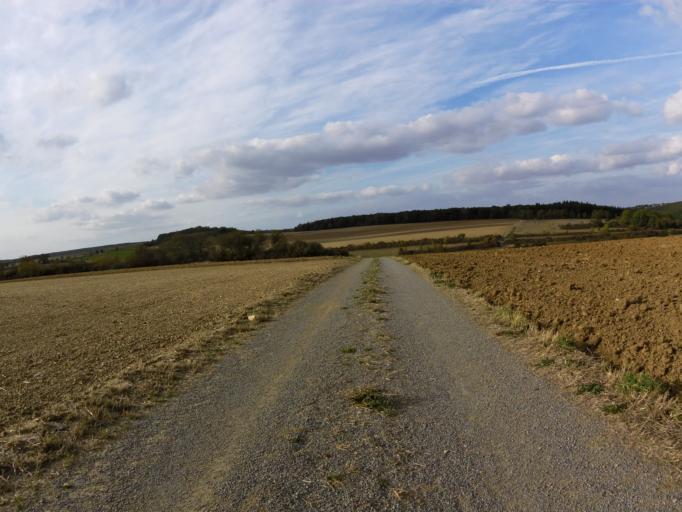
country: DE
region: Bavaria
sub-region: Regierungsbezirk Unterfranken
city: Reichenberg
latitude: 49.7282
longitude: 9.9444
